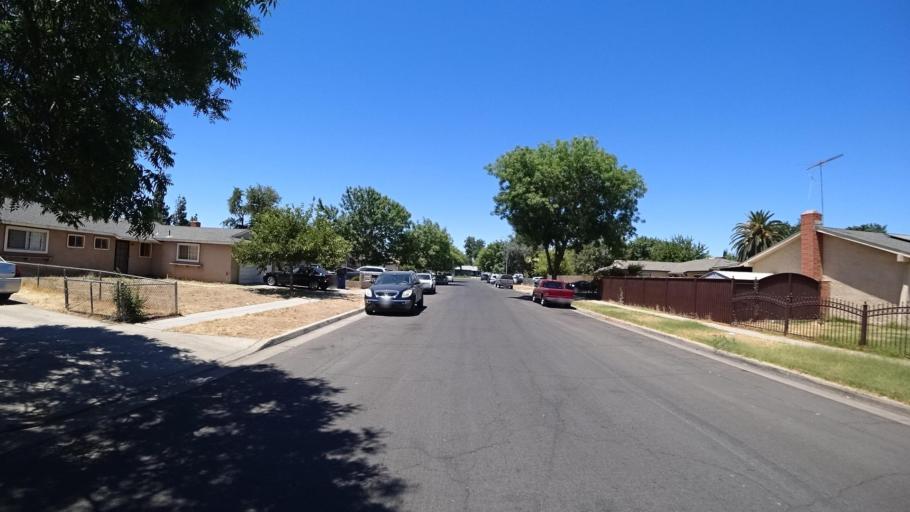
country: US
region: California
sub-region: Fresno County
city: Fresno
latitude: 36.7074
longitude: -119.7486
